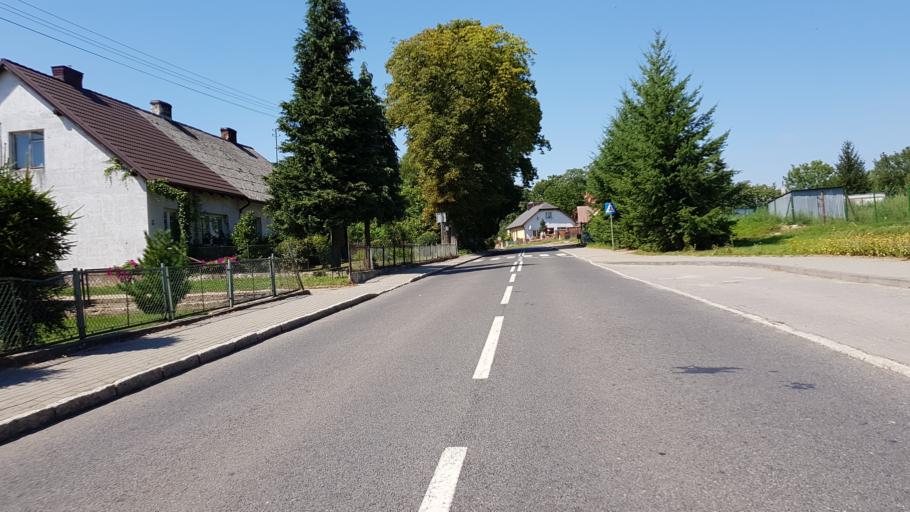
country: PL
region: West Pomeranian Voivodeship
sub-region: Powiat gryfinski
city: Banie
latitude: 53.1628
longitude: 14.5948
